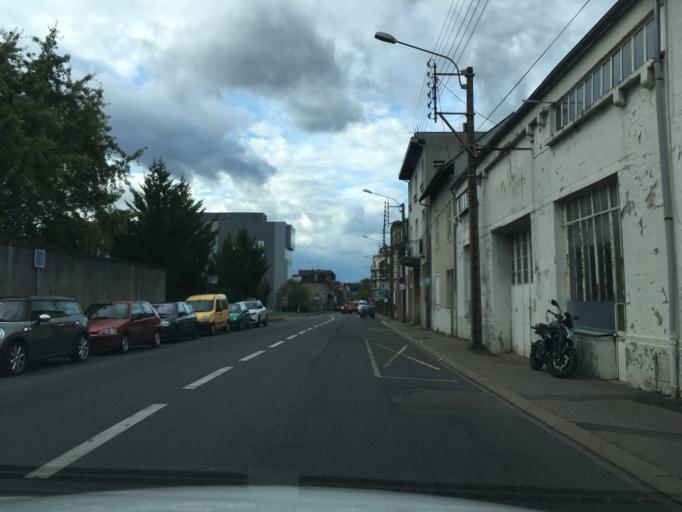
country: FR
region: Limousin
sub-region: Departement de la Correze
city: Brive-la-Gaillarde
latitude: 45.1531
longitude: 1.5394
